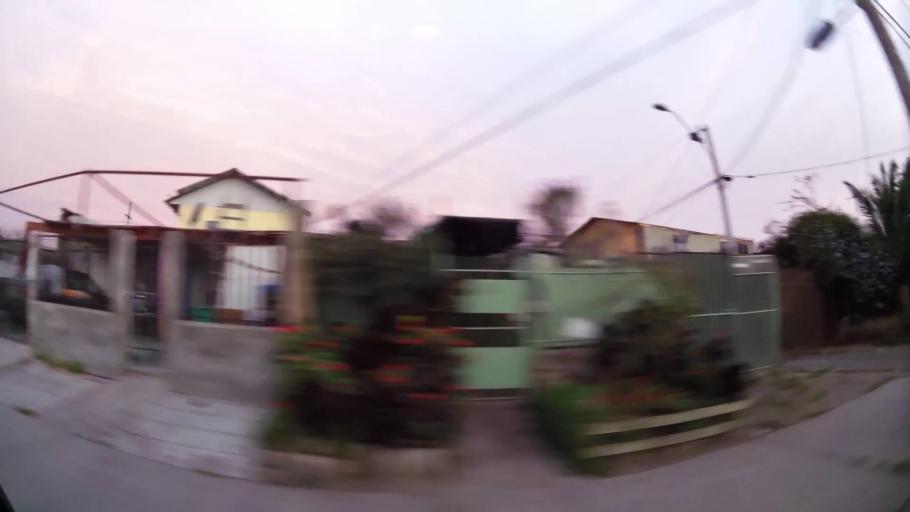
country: CL
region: Santiago Metropolitan
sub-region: Provincia de Santiago
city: Lo Prado
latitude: -33.4963
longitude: -70.7328
